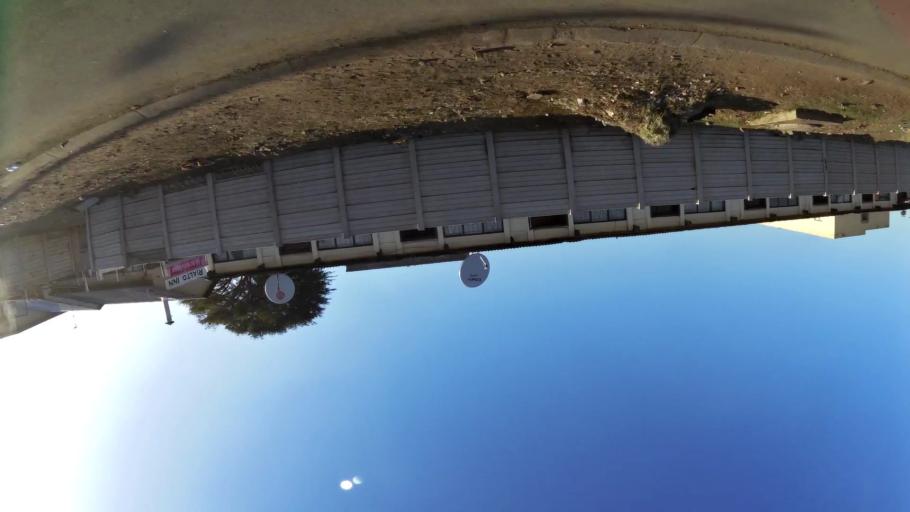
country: ZA
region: North-West
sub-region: Bojanala Platinum District Municipality
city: Rustenburg
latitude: -25.6436
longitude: 27.2142
